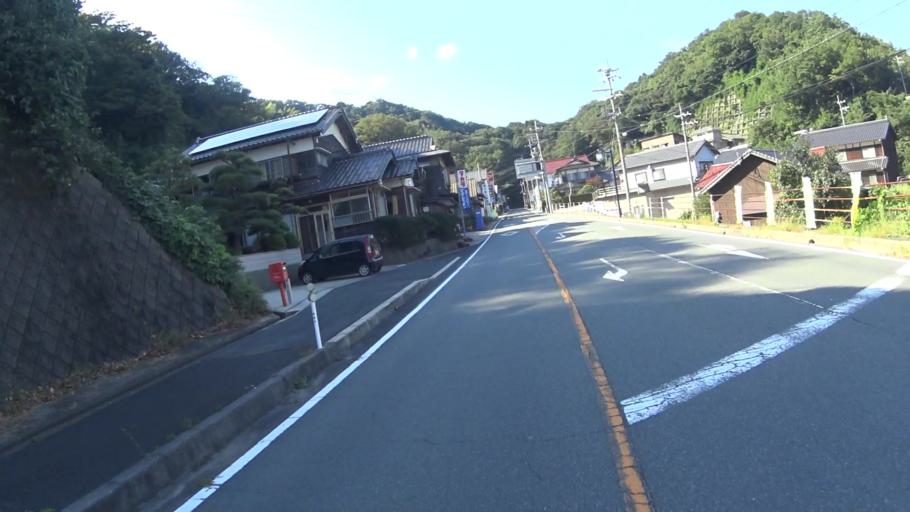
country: JP
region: Kyoto
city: Miyazu
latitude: 35.7310
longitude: 135.0957
